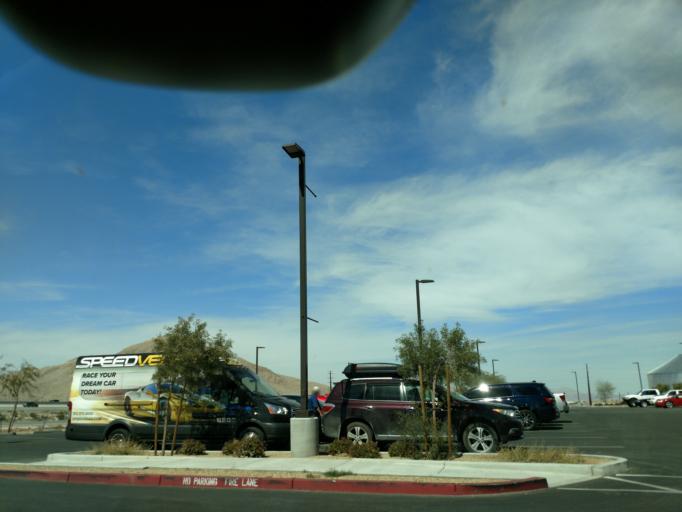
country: US
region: Nevada
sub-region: Clark County
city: Enterprise
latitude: 35.9336
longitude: -115.1889
